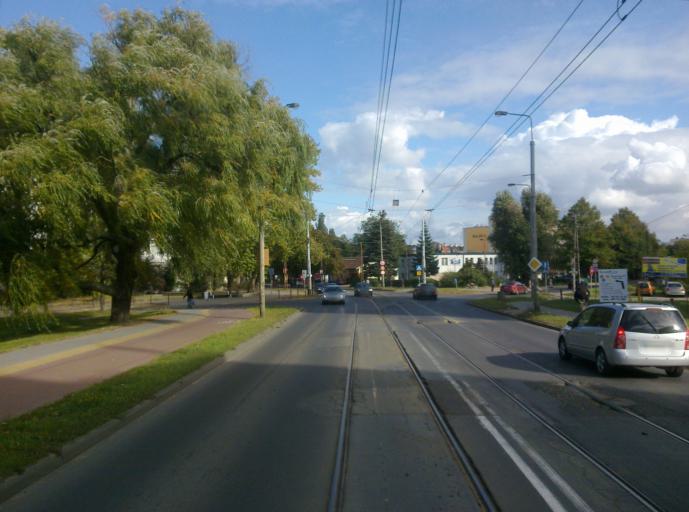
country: PL
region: Pomeranian Voivodeship
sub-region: Gdansk
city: Gdansk
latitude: 54.3567
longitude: 18.6809
